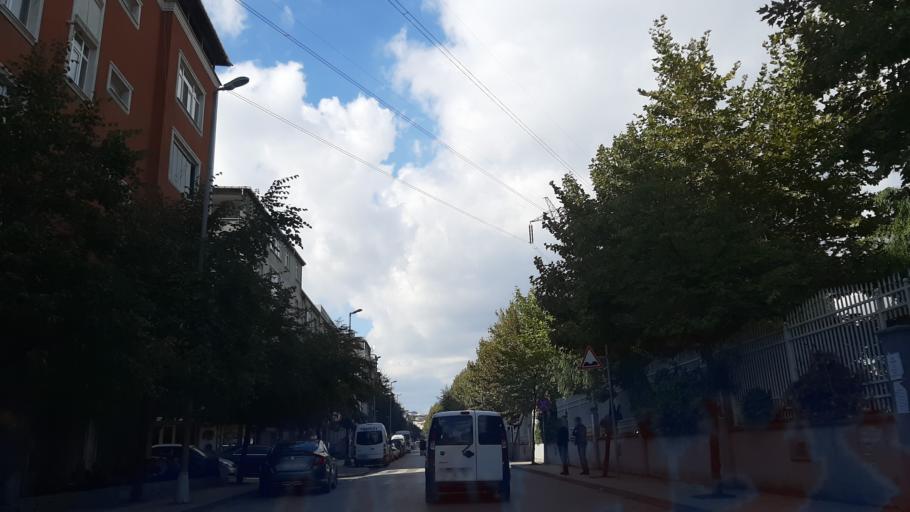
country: TR
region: Istanbul
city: Esenyurt
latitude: 41.0333
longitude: 28.6604
